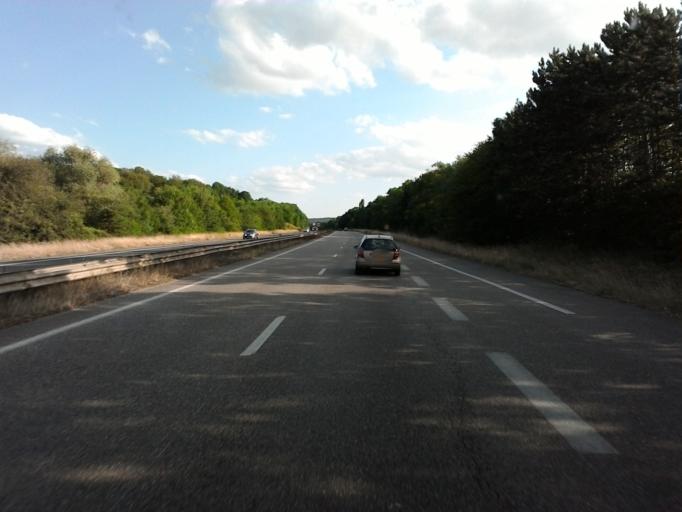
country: FR
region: Lorraine
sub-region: Departement de Meurthe-et-Moselle
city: Richardmenil
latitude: 48.6040
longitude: 6.1730
